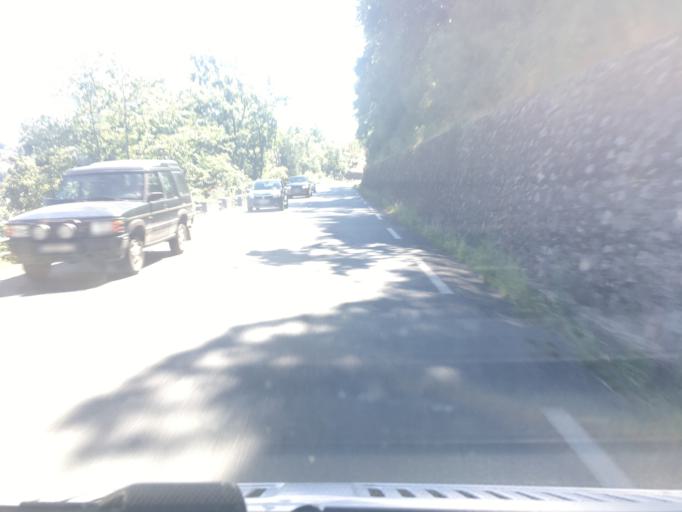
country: FR
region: Limousin
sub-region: Departement de la Correze
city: Bort-les-Orgues
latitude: 45.4067
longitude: 2.4980
